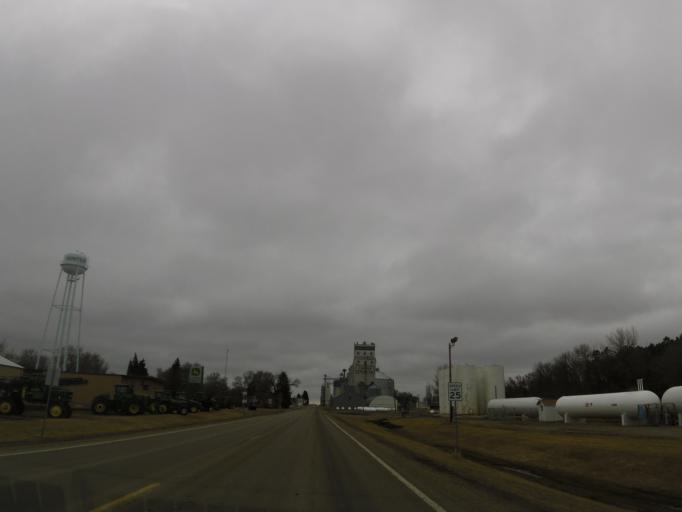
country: US
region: North Dakota
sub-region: Traill County
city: Hillsboro
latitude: 47.1942
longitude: -97.2174
